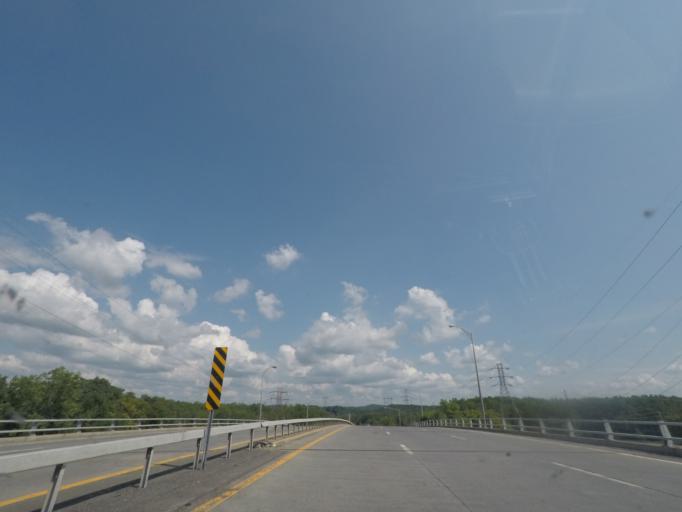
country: US
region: New York
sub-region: Albany County
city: Menands
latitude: 42.6850
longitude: -73.7291
